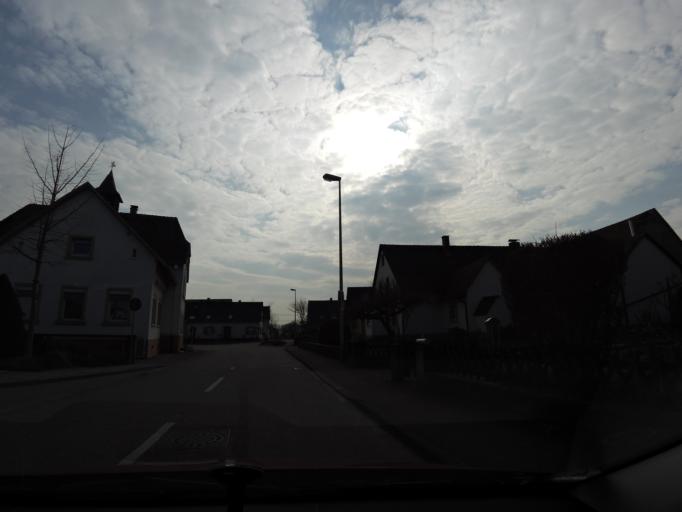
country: DE
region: Baden-Wuerttemberg
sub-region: Freiburg Region
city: Kehl
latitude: 48.5890
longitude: 7.8678
